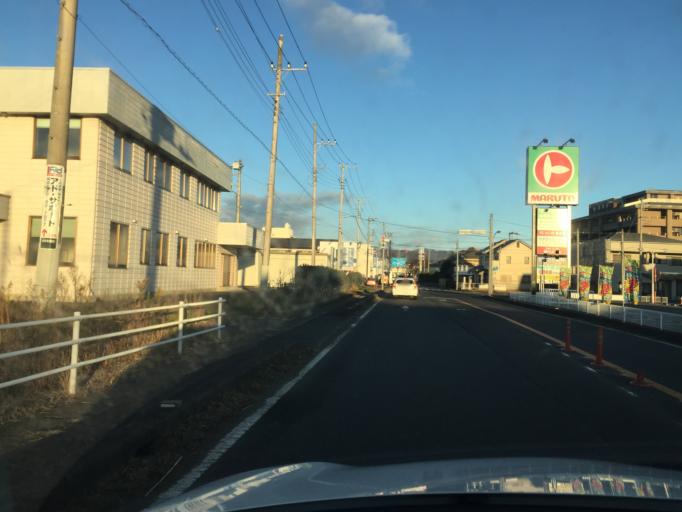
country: JP
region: Ibaraki
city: Kitaibaraki
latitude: 36.7891
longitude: 140.7407
